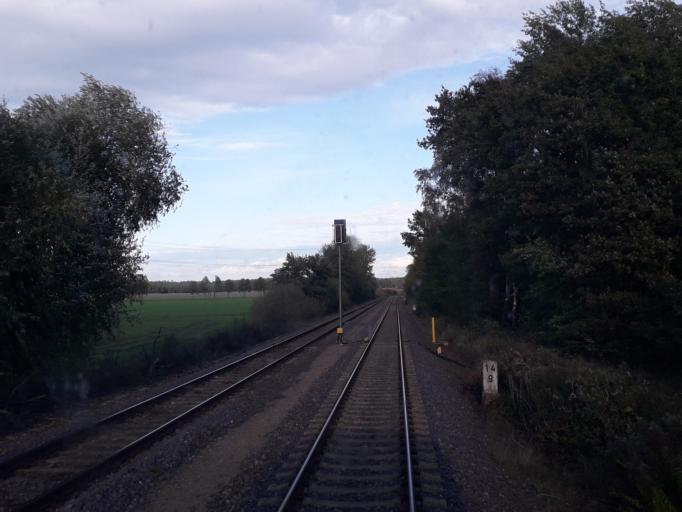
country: DE
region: Brandenburg
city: Perleberg
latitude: 53.0788
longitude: 11.9067
